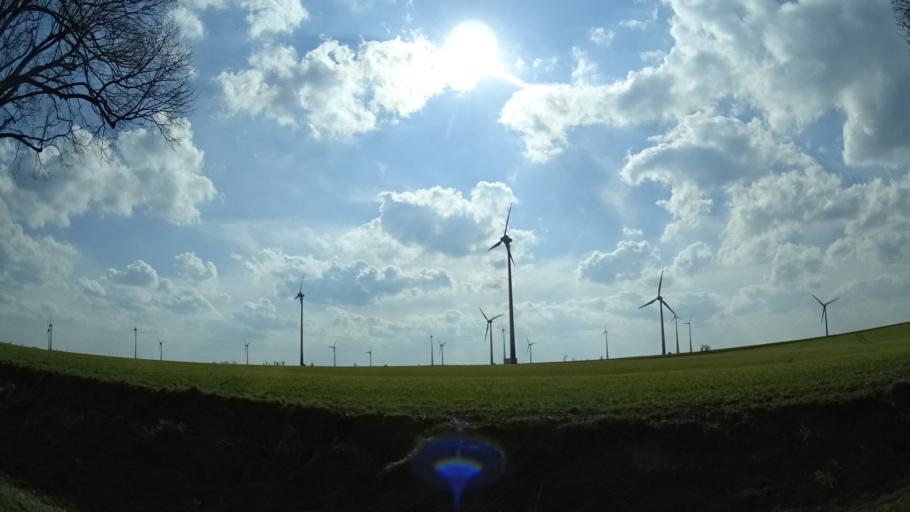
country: DE
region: Saxony-Anhalt
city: Stossen
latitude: 51.1081
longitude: 11.9316
